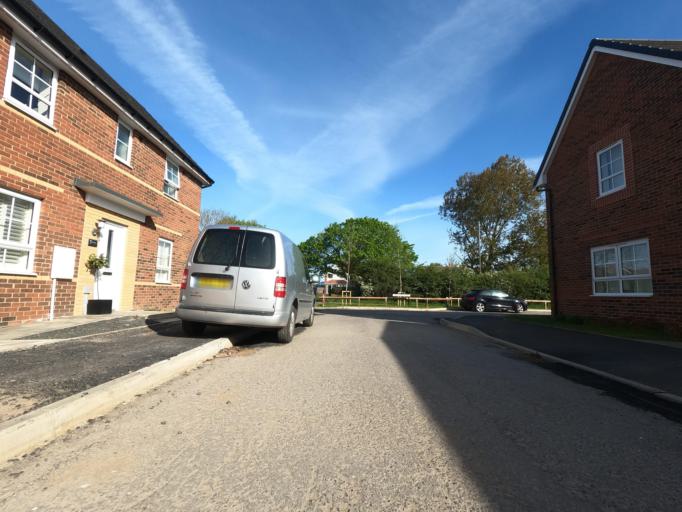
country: GB
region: England
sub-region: Northumberland
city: Morpeth
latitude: 55.1584
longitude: -1.6697
